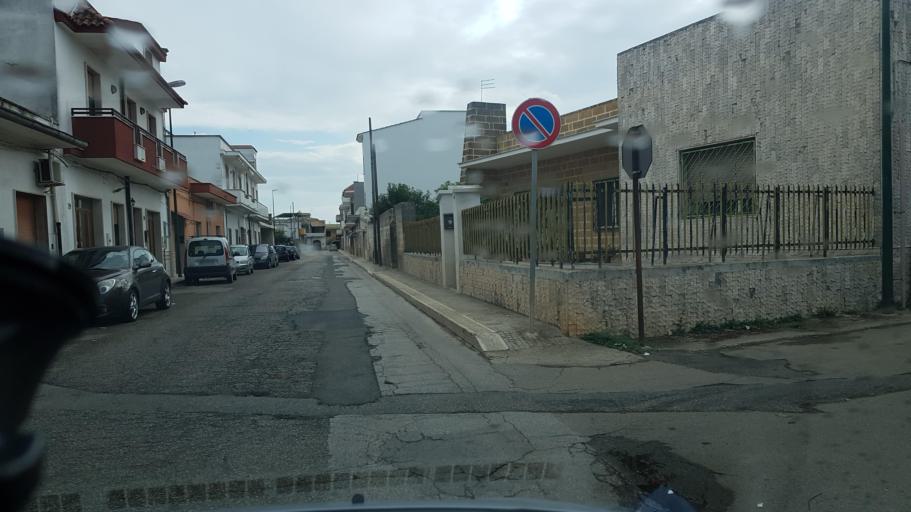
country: IT
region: Apulia
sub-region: Provincia di Brindisi
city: Torre Santa Susanna
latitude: 40.4625
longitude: 17.7441
